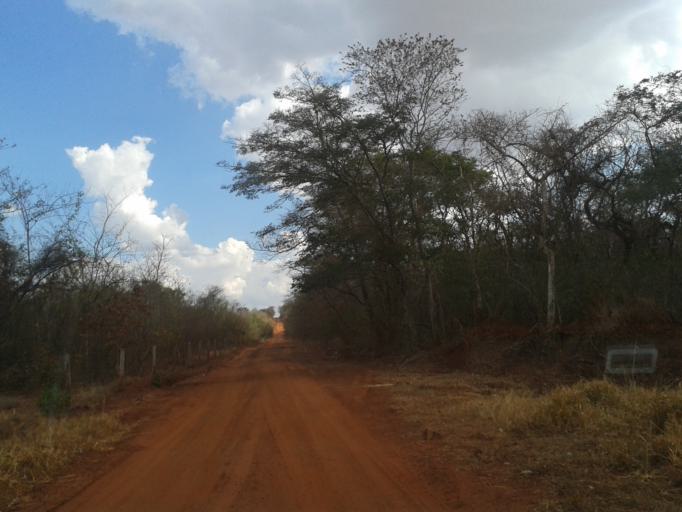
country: BR
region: Minas Gerais
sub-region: Santa Vitoria
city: Santa Vitoria
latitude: -19.2548
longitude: -49.9820
